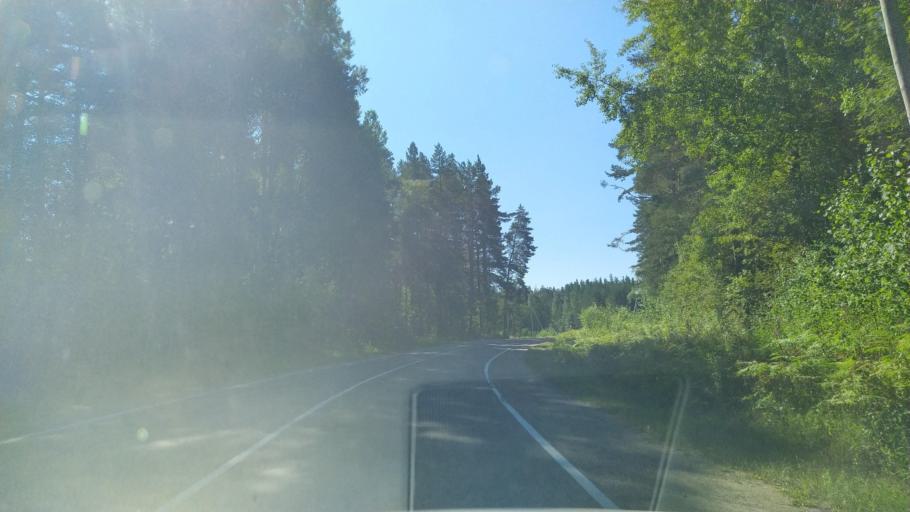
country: RU
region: Leningrad
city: Priozersk
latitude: 60.9927
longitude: 30.2567
